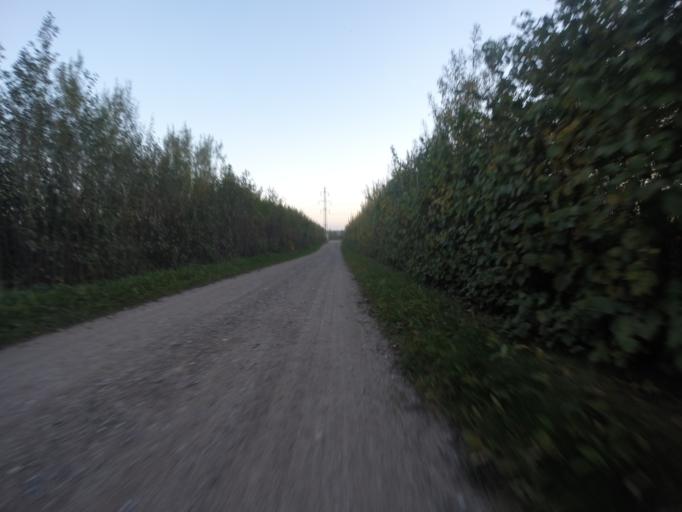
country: DK
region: Capital Region
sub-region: Hoje-Taastrup Kommune
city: Taastrup
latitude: 55.6735
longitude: 12.2960
